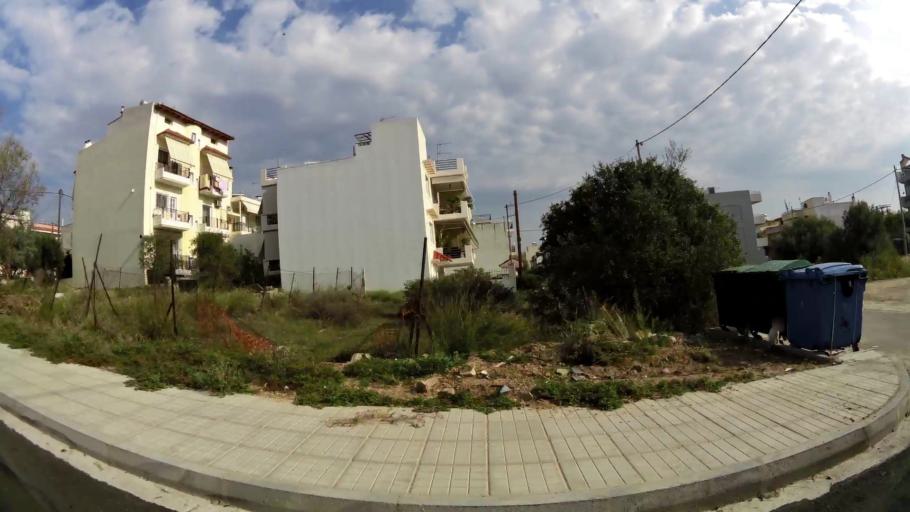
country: GR
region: Attica
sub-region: Nomarchia Athinas
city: Kamateron
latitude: 38.0510
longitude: 23.6987
